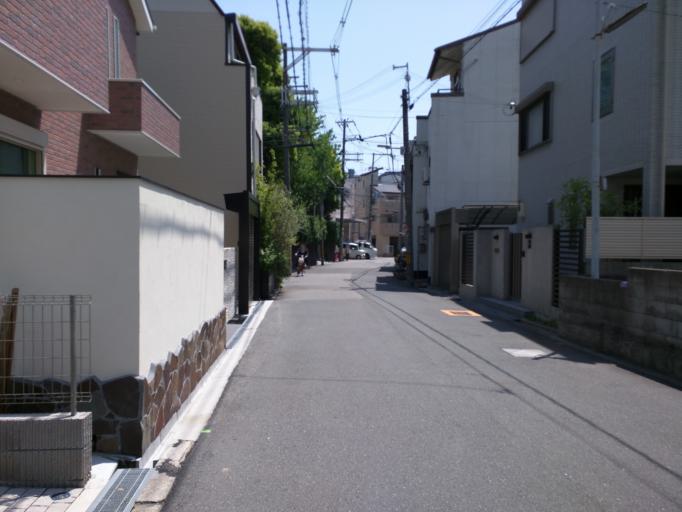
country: JP
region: Osaka
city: Osaka-shi
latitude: 34.6883
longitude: 135.4785
